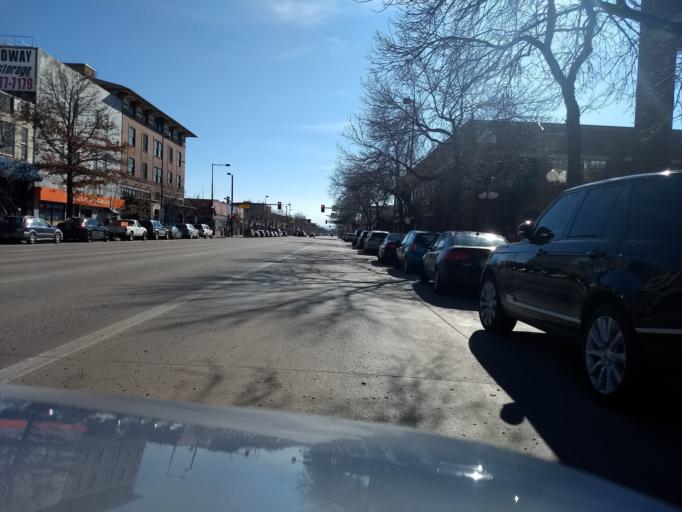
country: US
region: Colorado
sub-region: Denver County
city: Denver
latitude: 39.7173
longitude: -104.9876
